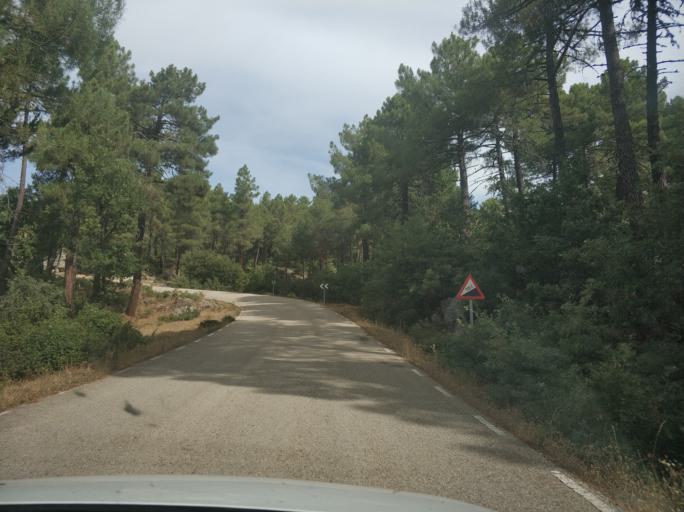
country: ES
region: Castille and Leon
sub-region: Provincia de Soria
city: Duruelo de la Sierra
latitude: 41.8937
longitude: -2.9452
